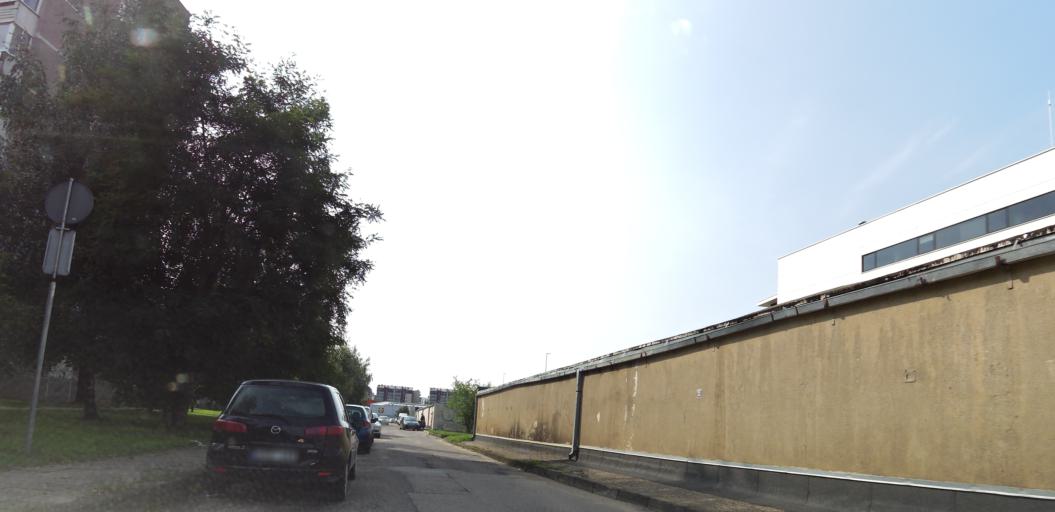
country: LT
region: Vilnius County
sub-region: Vilnius
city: Fabijoniskes
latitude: 54.7399
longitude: 25.2353
